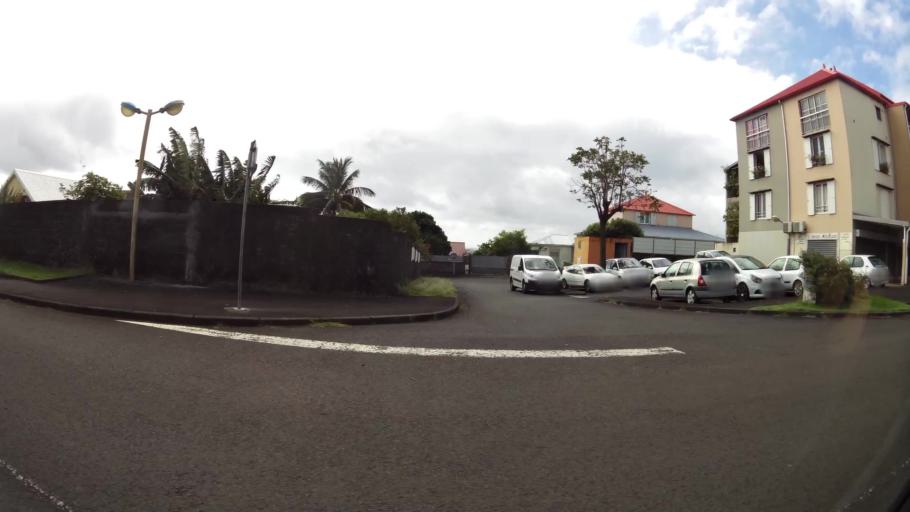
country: RE
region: Reunion
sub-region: Reunion
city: Sainte-Marie
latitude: -20.8957
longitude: 55.5675
